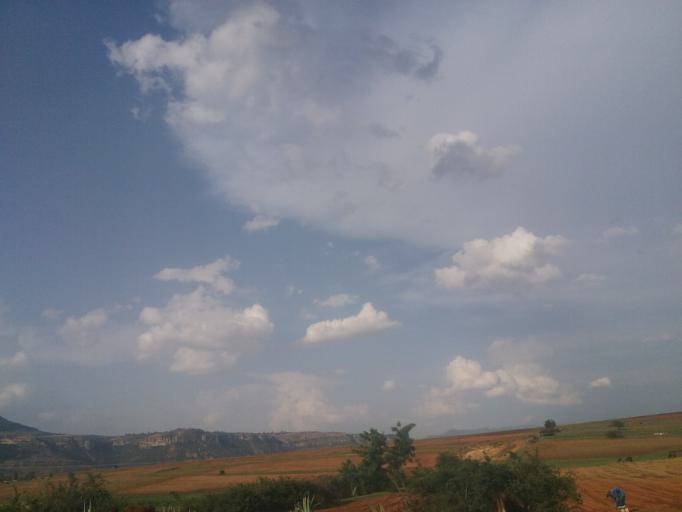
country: LS
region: Leribe
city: Leribe
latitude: -28.9293
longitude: 28.1352
